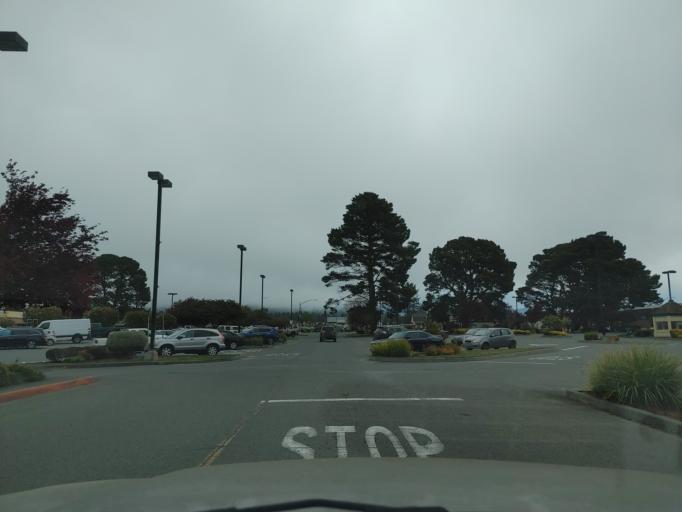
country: US
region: California
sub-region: Humboldt County
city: McKinleyville
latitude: 40.9431
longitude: -124.1030
